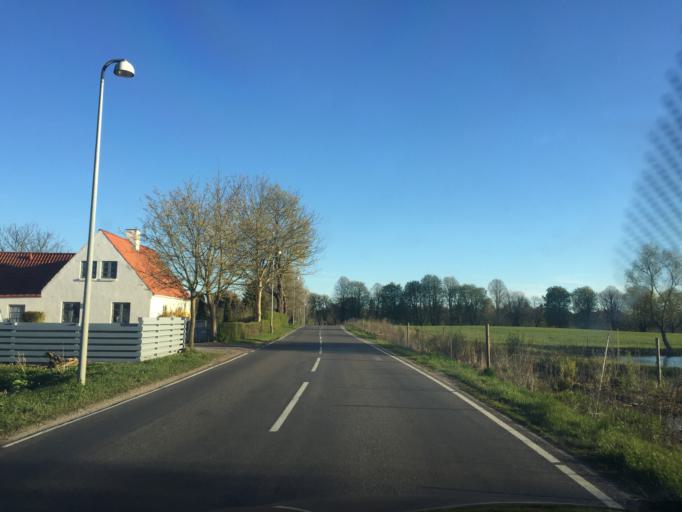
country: DK
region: Capital Region
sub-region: Hoje-Taastrup Kommune
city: Taastrup
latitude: 55.6898
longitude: 12.2455
